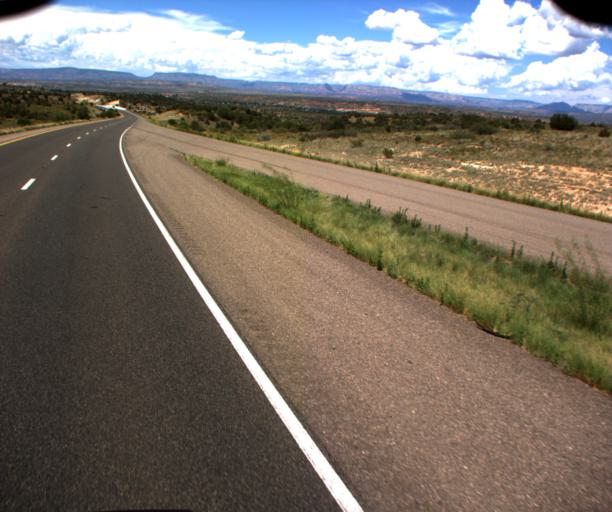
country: US
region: Arizona
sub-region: Yavapai County
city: Verde Village
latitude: 34.6653
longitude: -111.9676
